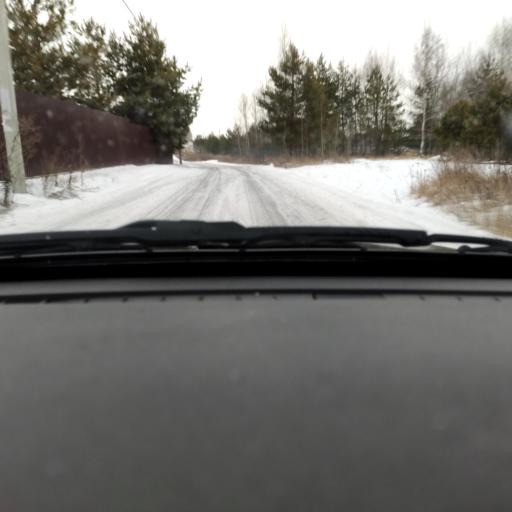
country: RU
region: Voronezj
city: Ramon'
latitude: 51.8934
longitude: 39.2563
